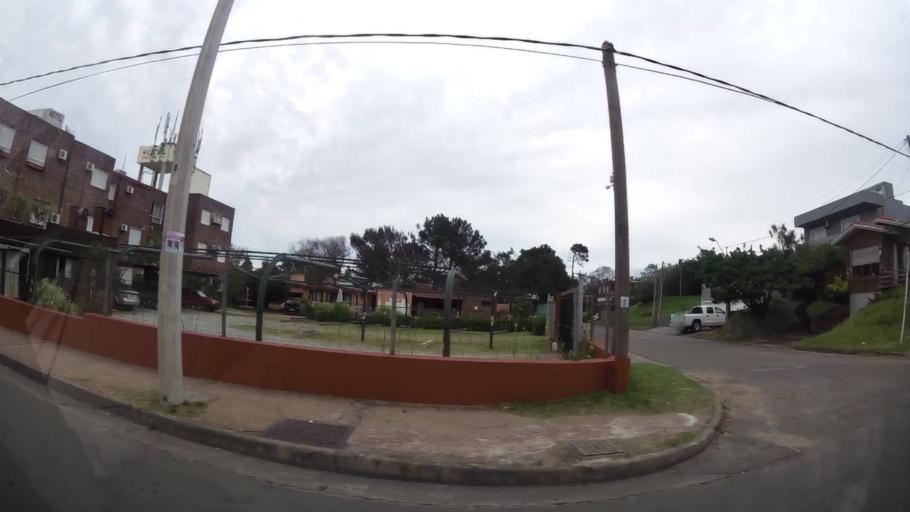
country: UY
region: Maldonado
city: Maldonado
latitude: -34.9180
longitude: -54.9711
